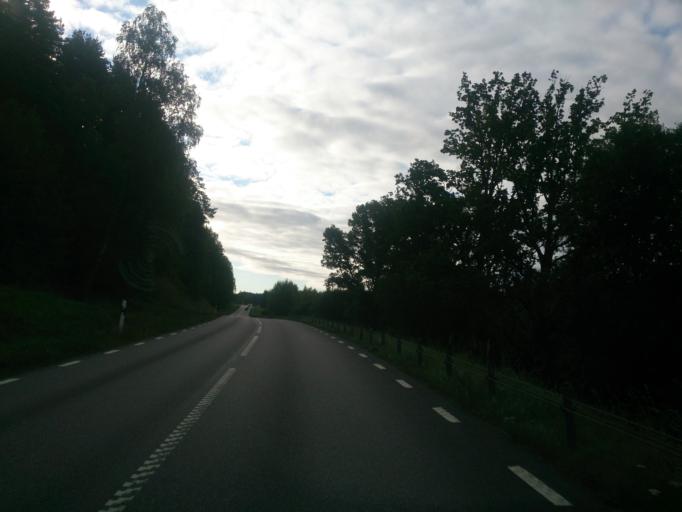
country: SE
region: OEstergoetland
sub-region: Atvidabergs Kommun
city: Atvidaberg
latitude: 58.2811
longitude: 15.9040
